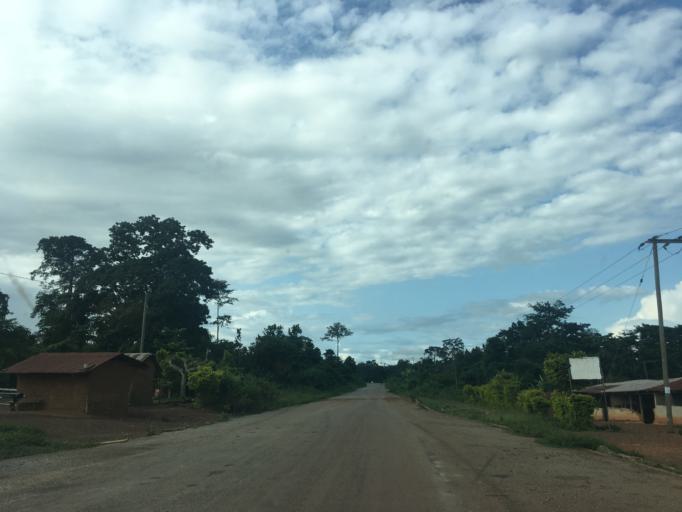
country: GH
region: Western
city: Wassa-Akropong
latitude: 6.0083
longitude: -2.4066
